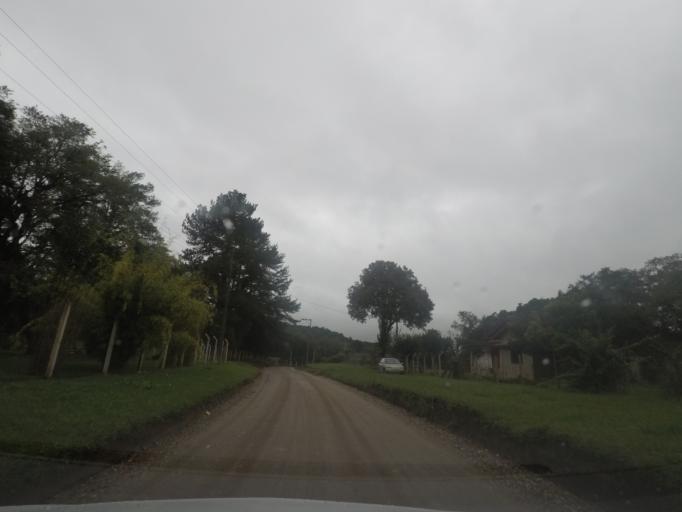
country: BR
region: Parana
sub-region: Campina Grande Do Sul
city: Campina Grande do Sul
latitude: -25.3052
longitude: -49.1128
